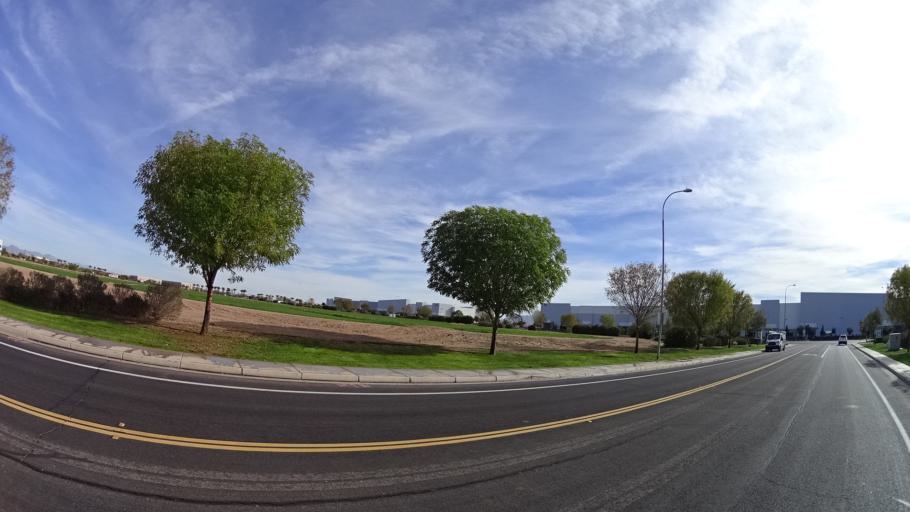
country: US
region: Arizona
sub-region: Maricopa County
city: Chandler
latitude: 33.2782
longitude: -111.8134
